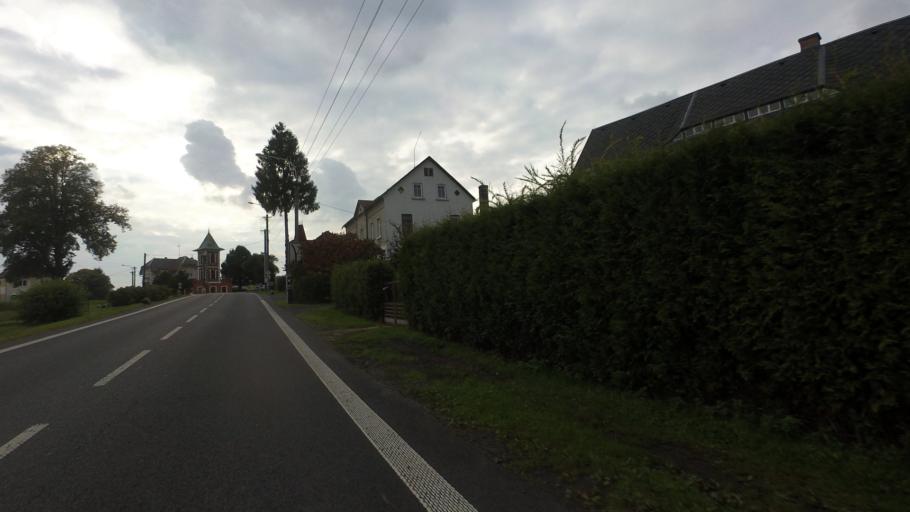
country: CZ
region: Ustecky
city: Vilemov
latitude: 51.0195
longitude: 14.3150
